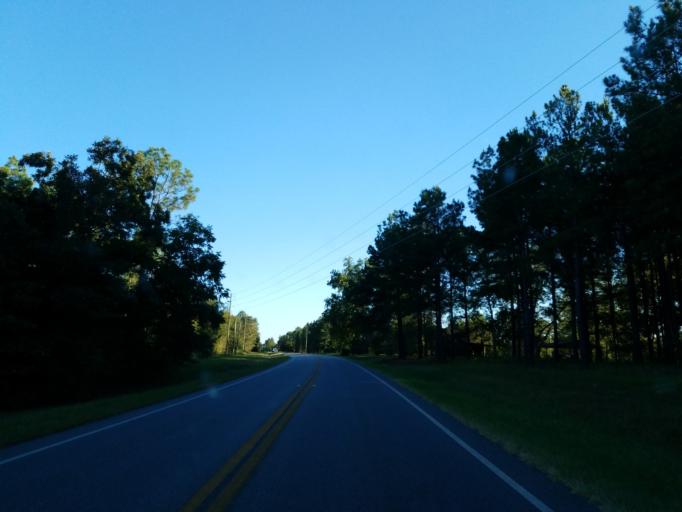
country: US
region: Georgia
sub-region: Worth County
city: Sylvester
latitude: 31.5905
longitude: -83.8633
